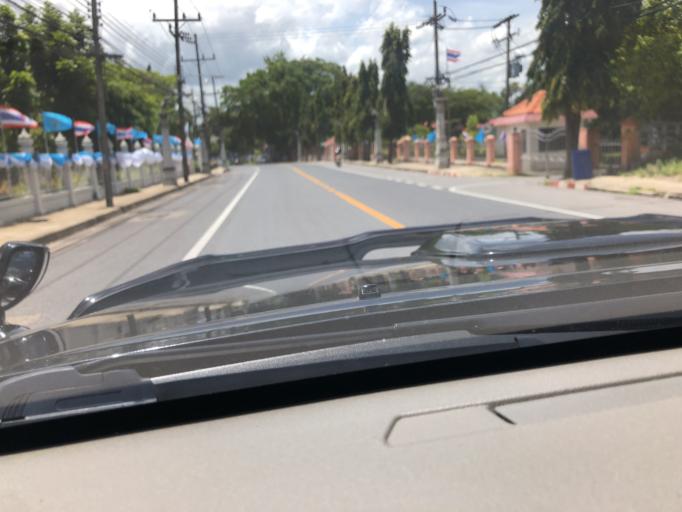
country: TH
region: Krabi
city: Krabi
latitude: 8.0585
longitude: 98.9184
